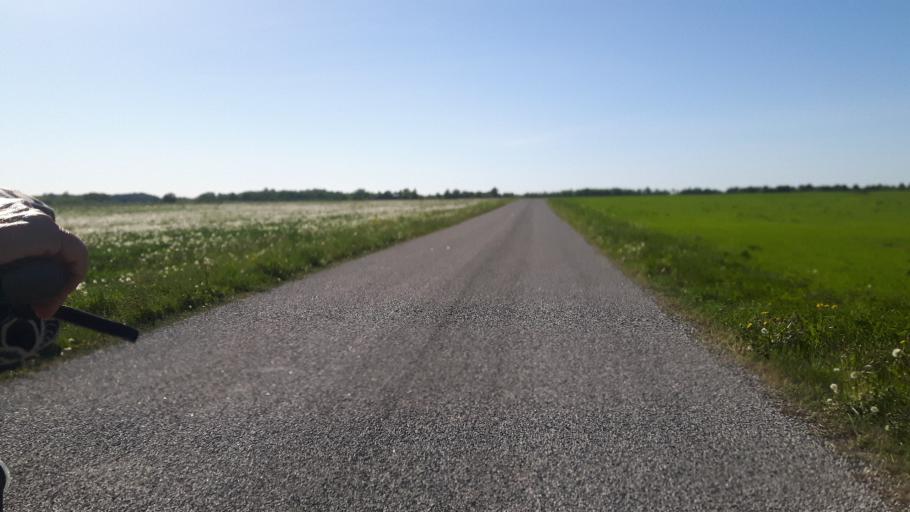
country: EE
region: Ida-Virumaa
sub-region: Kohtla-Jaerve linn
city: Kohtla-Jarve
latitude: 59.4328
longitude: 27.2117
